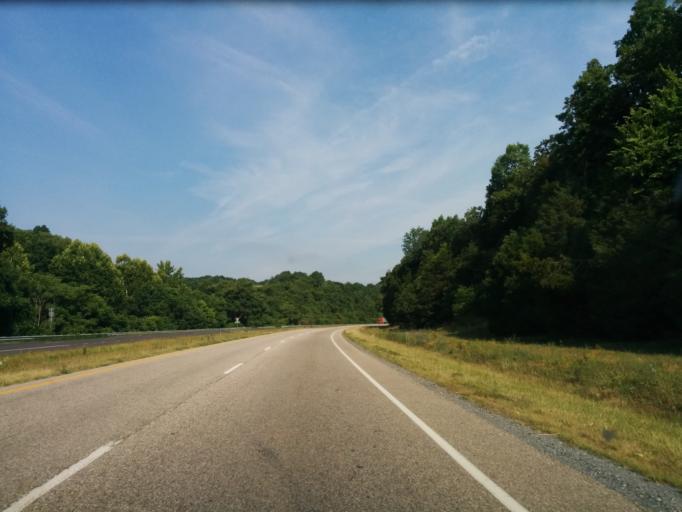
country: US
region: Virginia
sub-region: City of Lexington
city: Lexington
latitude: 37.7596
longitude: -79.4207
